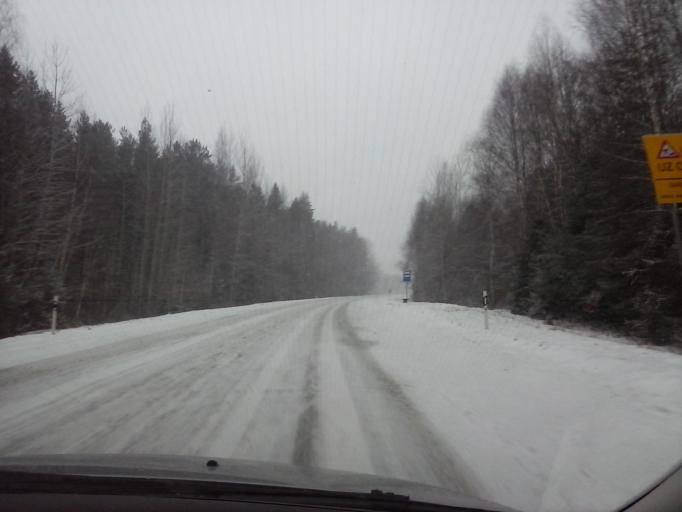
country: LV
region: Valkas Rajons
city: Valka
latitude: 57.7131
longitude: 25.9272
